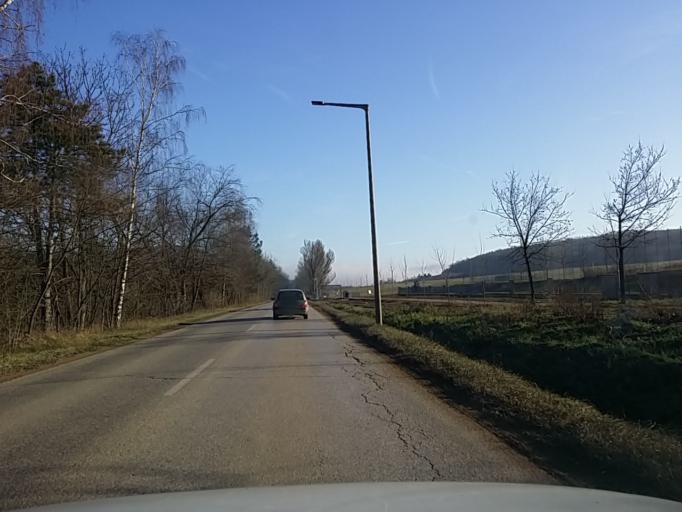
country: HU
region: Pest
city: Solymar
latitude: 47.5701
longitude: 18.9027
